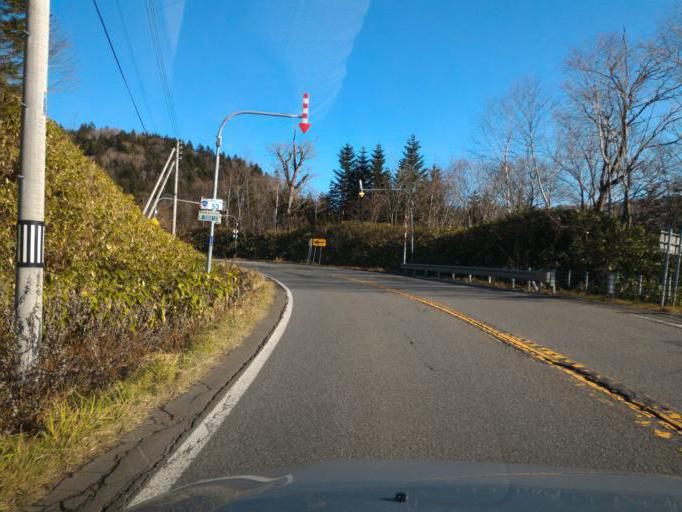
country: JP
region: Hokkaido
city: Bibai
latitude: 43.2792
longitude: 142.0585
